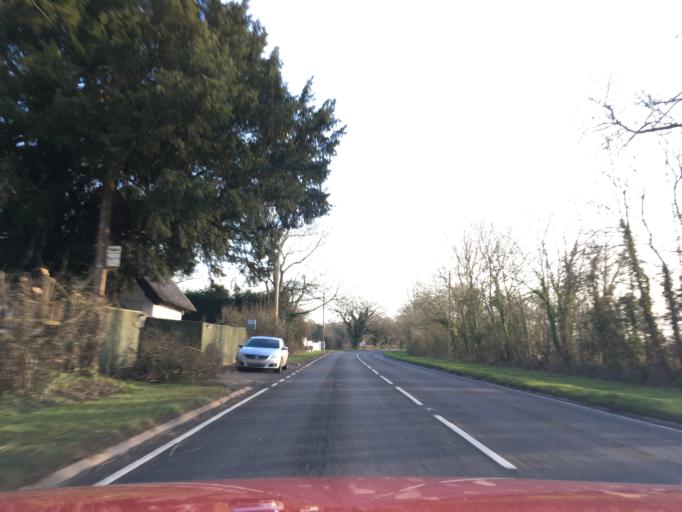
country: GB
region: England
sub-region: Warwickshire
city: Henley in Arden
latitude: 52.2568
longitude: -1.7623
